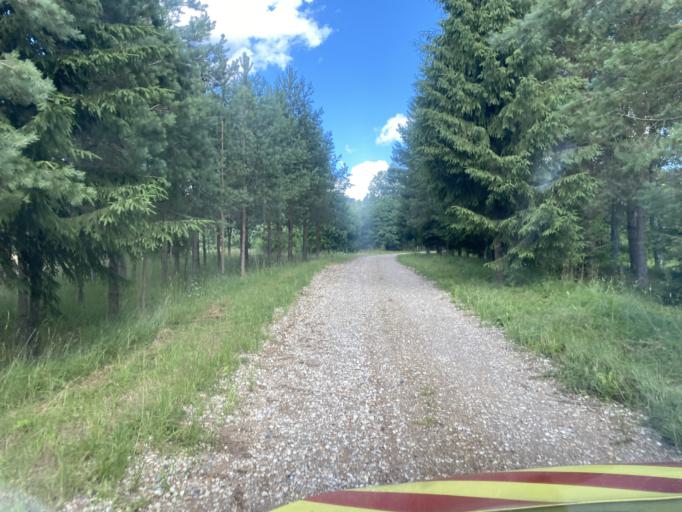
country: EE
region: Viljandimaa
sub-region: Viljandi linn
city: Viljandi
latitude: 58.2867
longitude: 25.5876
